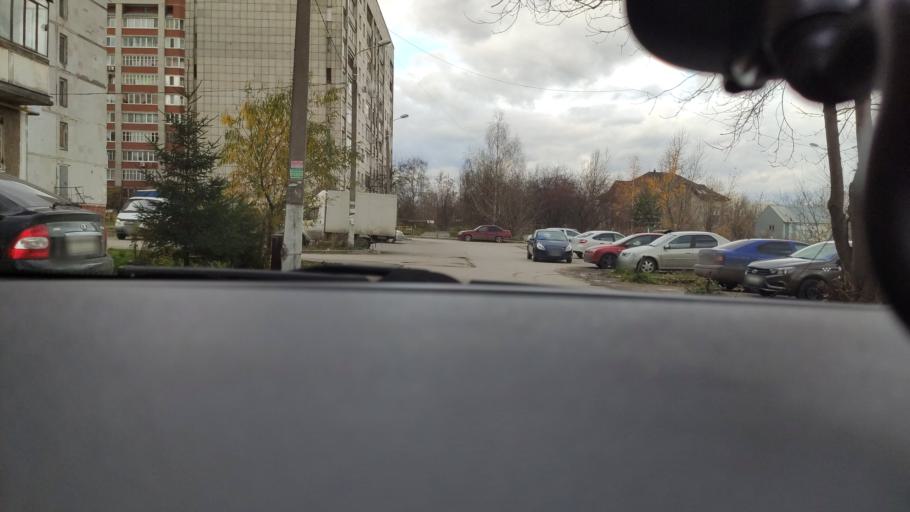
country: RU
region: Perm
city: Perm
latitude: 57.9798
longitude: 56.2799
